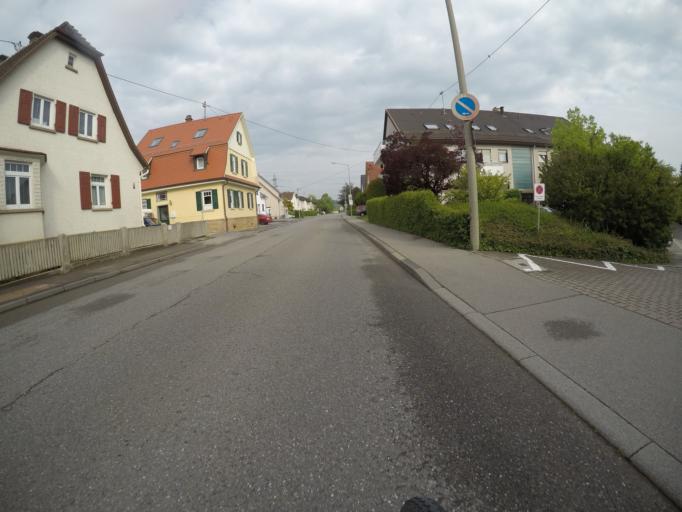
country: DE
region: Baden-Wuerttemberg
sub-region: Regierungsbezirk Stuttgart
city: Magstadt
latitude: 48.7446
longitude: 8.9562
